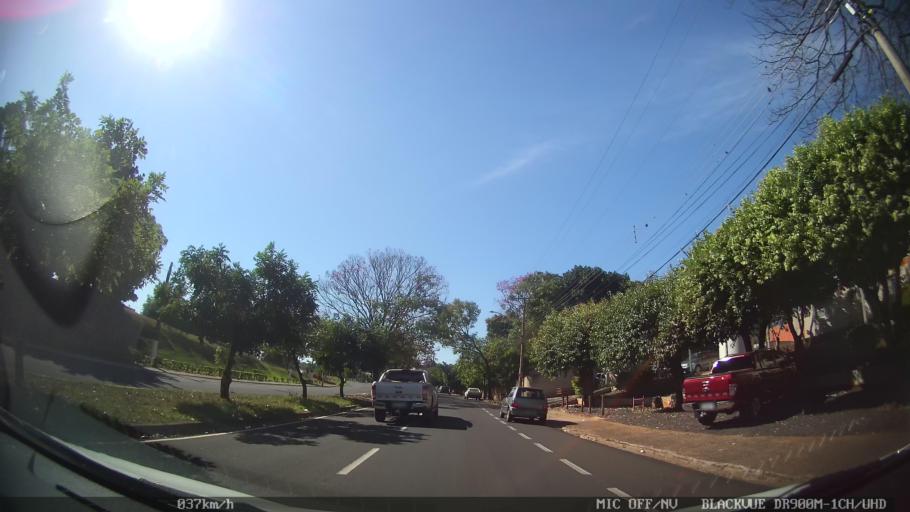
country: BR
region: Sao Paulo
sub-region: Sao Jose Do Rio Preto
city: Sao Jose do Rio Preto
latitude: -20.8149
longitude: -49.4326
